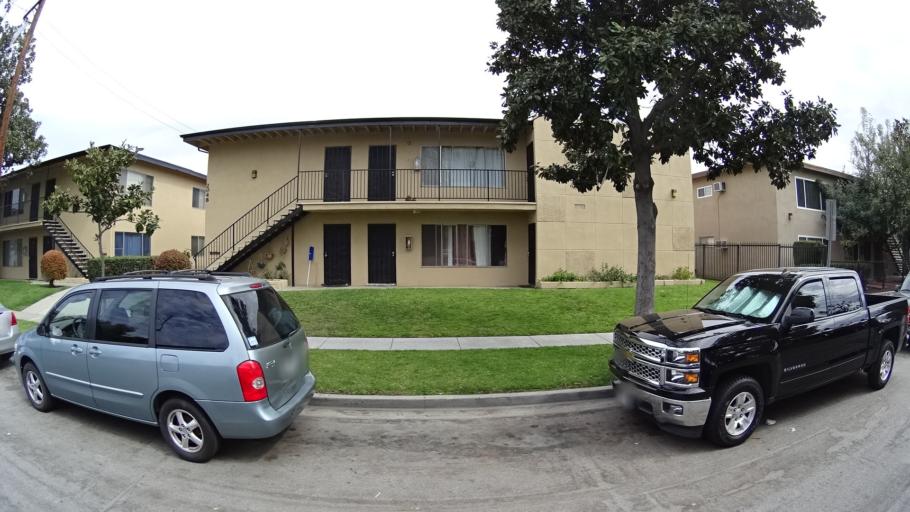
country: US
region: California
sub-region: Orange County
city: Anaheim
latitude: 33.7977
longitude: -117.8994
